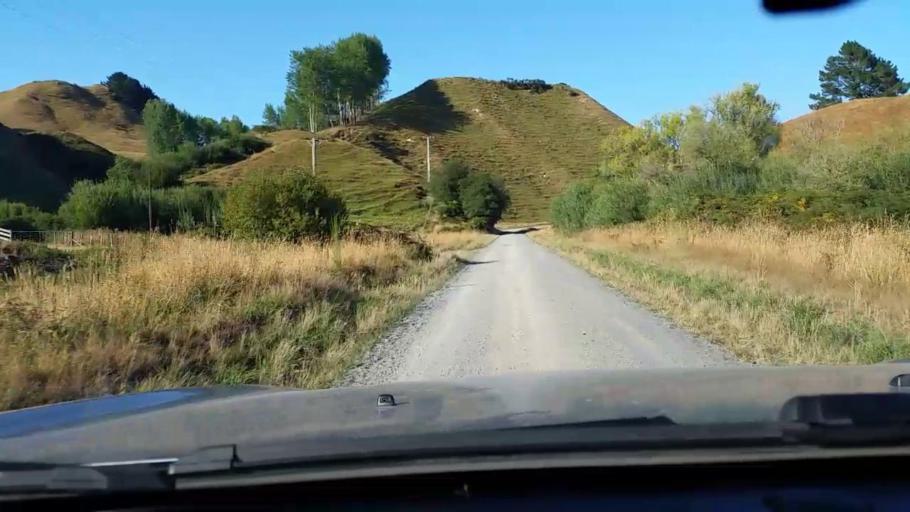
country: NZ
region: Waikato
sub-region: Taupo District
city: Taupo
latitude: -38.4748
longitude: 176.2232
